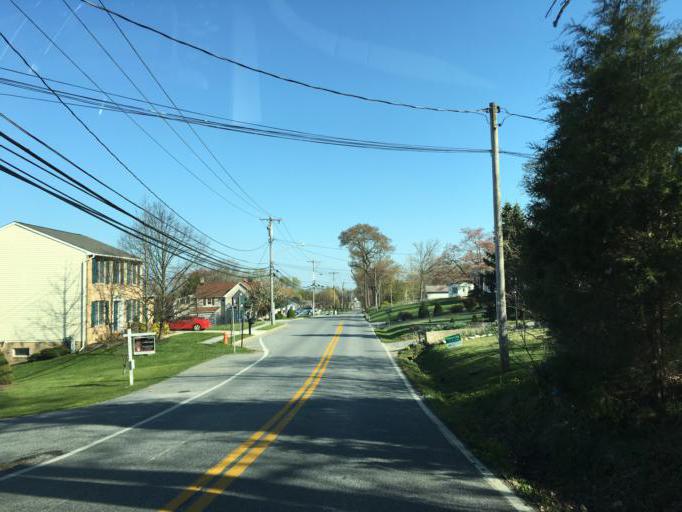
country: US
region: Maryland
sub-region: Baltimore County
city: Perry Hall
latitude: 39.4024
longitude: -76.4908
